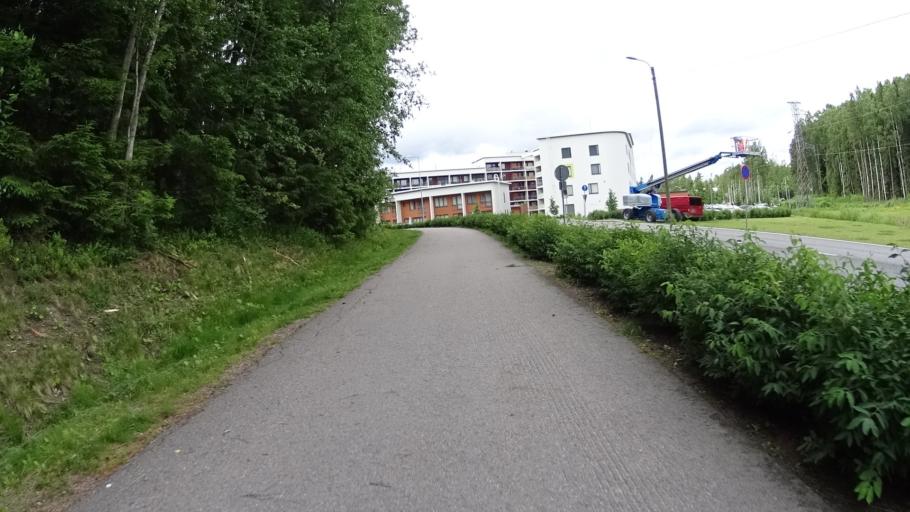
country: FI
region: Uusimaa
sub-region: Helsinki
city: Kilo
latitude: 60.2528
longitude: 24.7988
